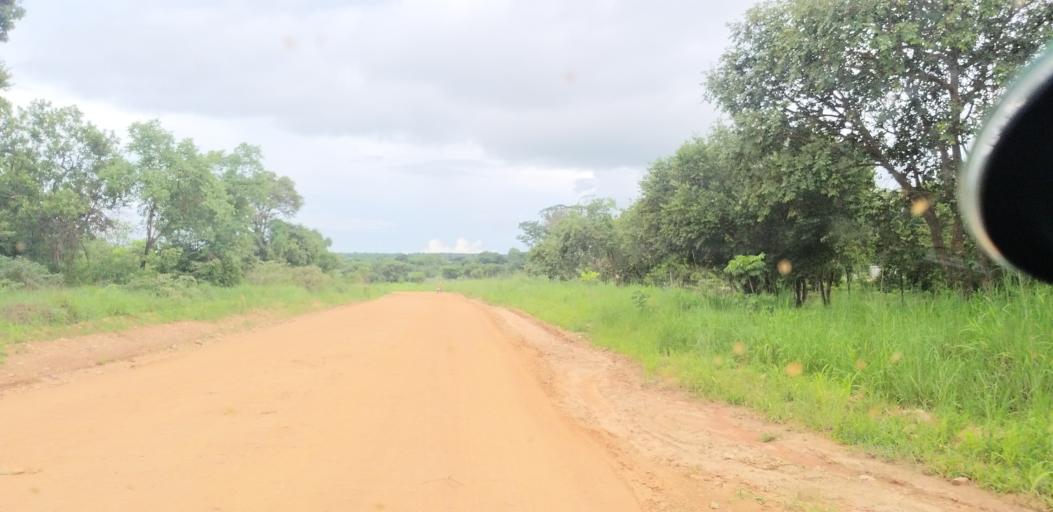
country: ZM
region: Lusaka
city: Lusaka
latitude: -15.1976
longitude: 28.4416
